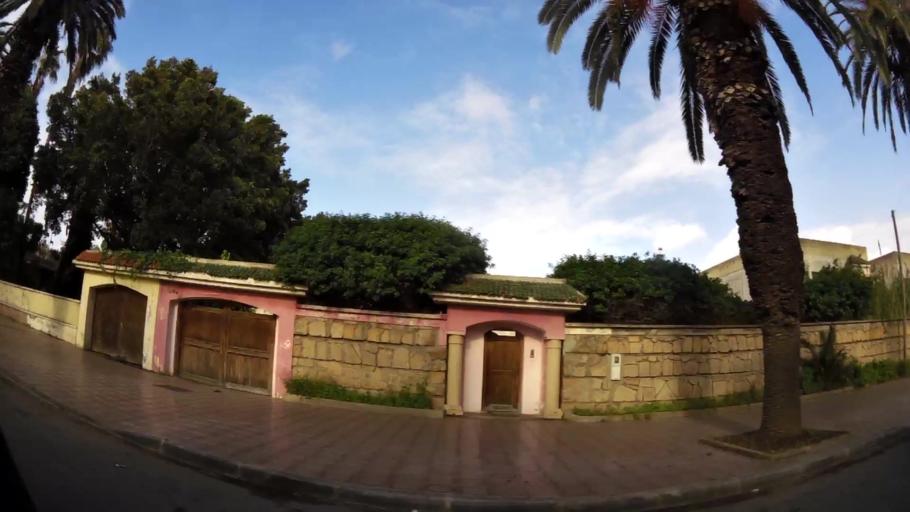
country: MA
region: Grand Casablanca
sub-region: Mohammedia
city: Mohammedia
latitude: 33.7025
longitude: -7.3942
